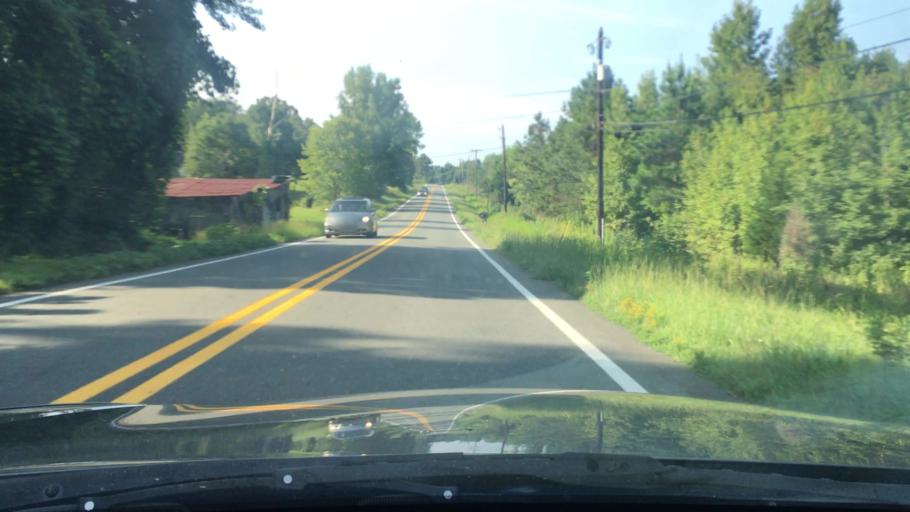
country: US
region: North Carolina
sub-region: Alamance County
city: Green Level
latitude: 36.2346
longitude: -79.3224
